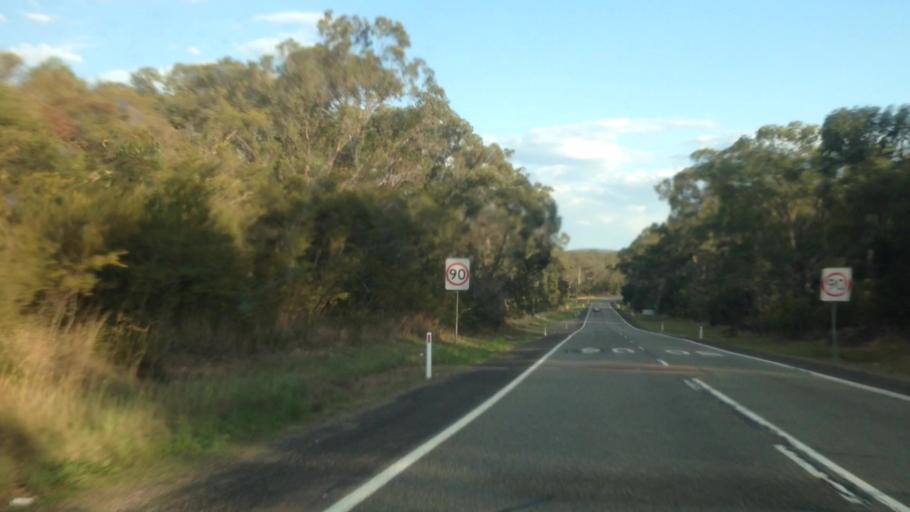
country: AU
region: New South Wales
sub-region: Cessnock
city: Kurri Kurri
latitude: -32.8354
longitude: 151.4811
